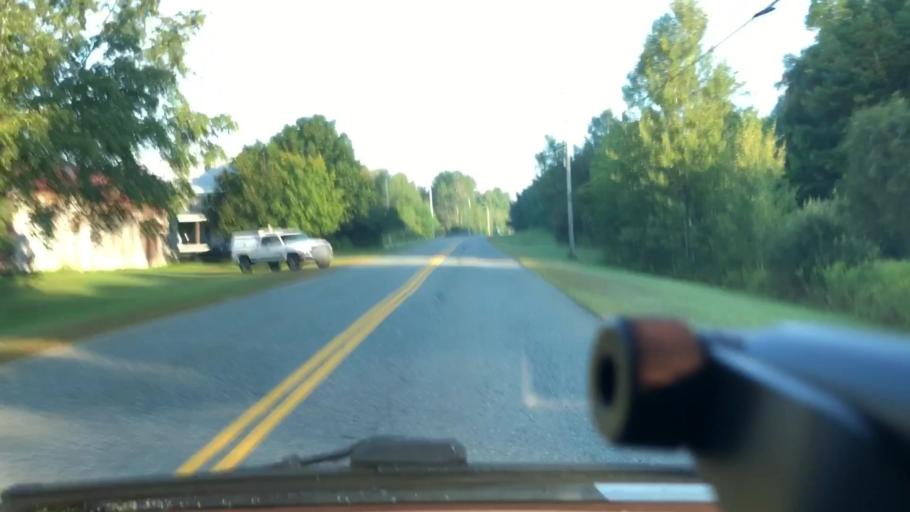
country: US
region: Massachusetts
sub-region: Franklin County
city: Ashfield
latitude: 42.5043
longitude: -72.8799
